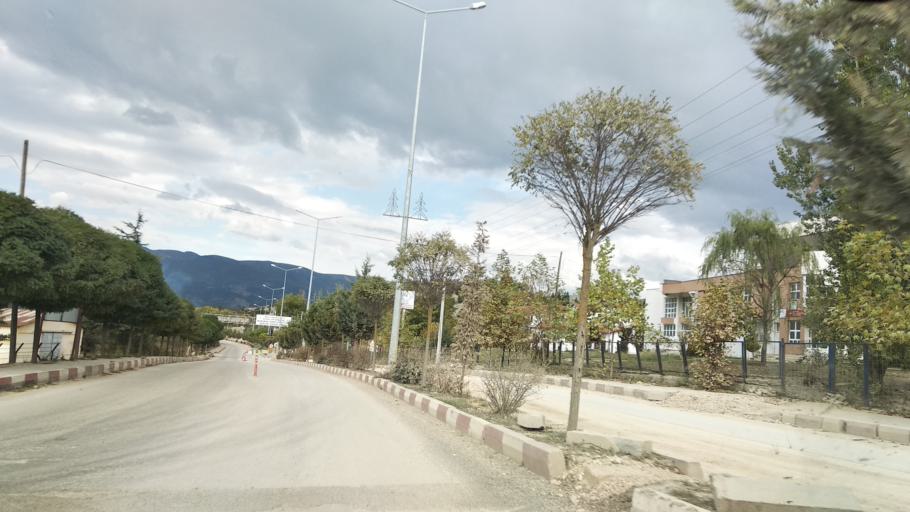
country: TR
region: Bolu
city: Mudurnu
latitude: 40.4773
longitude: 31.2105
